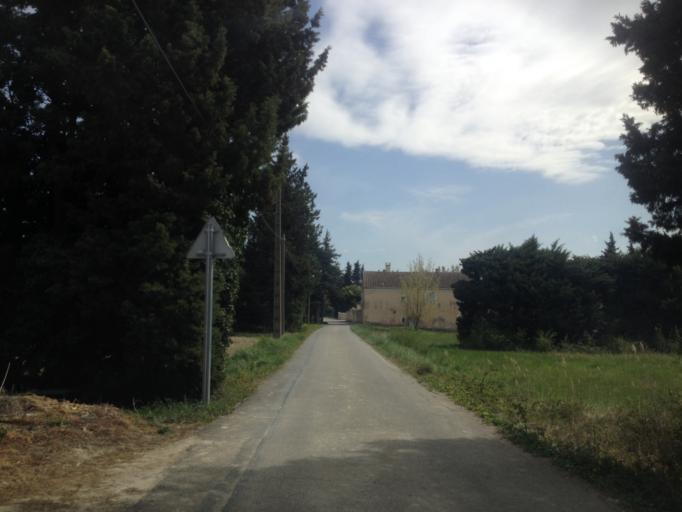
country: FR
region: Provence-Alpes-Cote d'Azur
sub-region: Departement du Vaucluse
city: Caderousse
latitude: 44.1170
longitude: 4.7810
